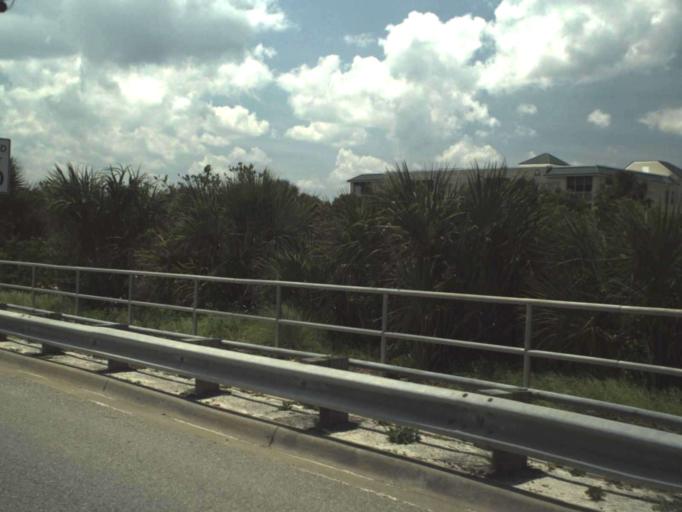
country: US
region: Florida
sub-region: Volusia County
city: New Smyrna Beach
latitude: 29.0288
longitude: -80.9047
